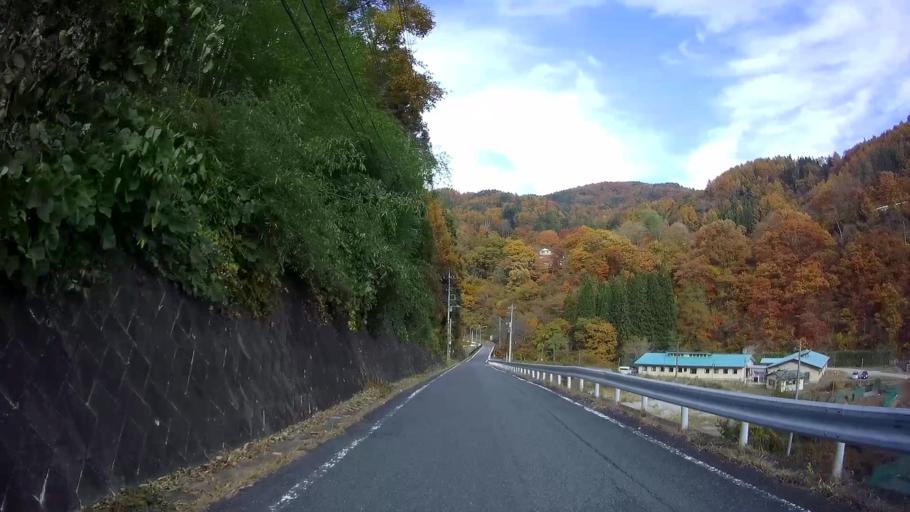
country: JP
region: Gunma
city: Nakanojomachi
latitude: 36.6384
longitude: 138.6492
